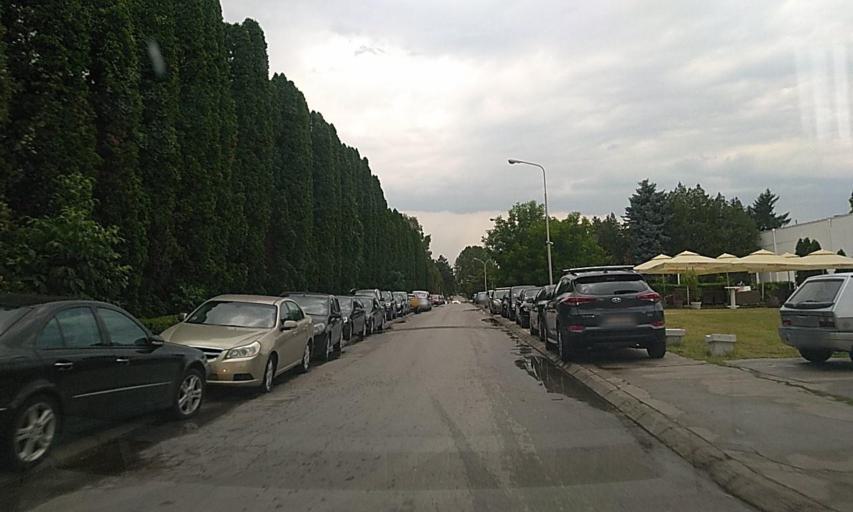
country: RS
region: Central Serbia
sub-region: Nisavski Okrug
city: Nis
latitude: 43.3057
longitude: 21.9502
